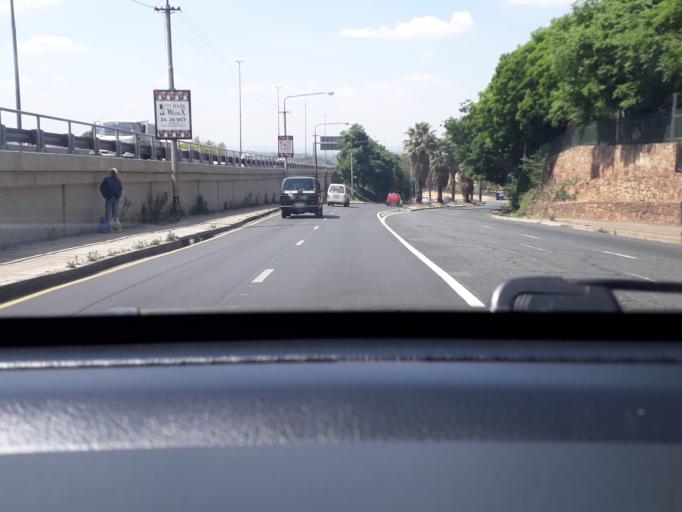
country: ZA
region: Gauteng
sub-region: City of Johannesburg Metropolitan Municipality
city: Johannesburg
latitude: -26.1774
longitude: 28.0376
